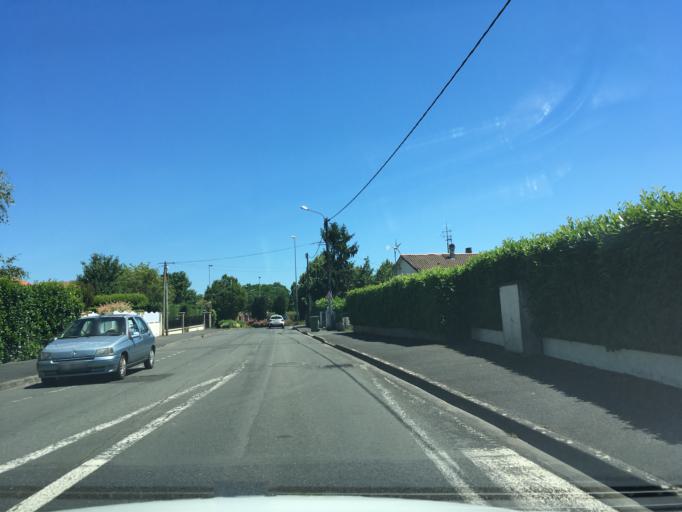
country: FR
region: Poitou-Charentes
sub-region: Departement des Deux-Sevres
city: Niort
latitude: 46.3413
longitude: -0.4403
